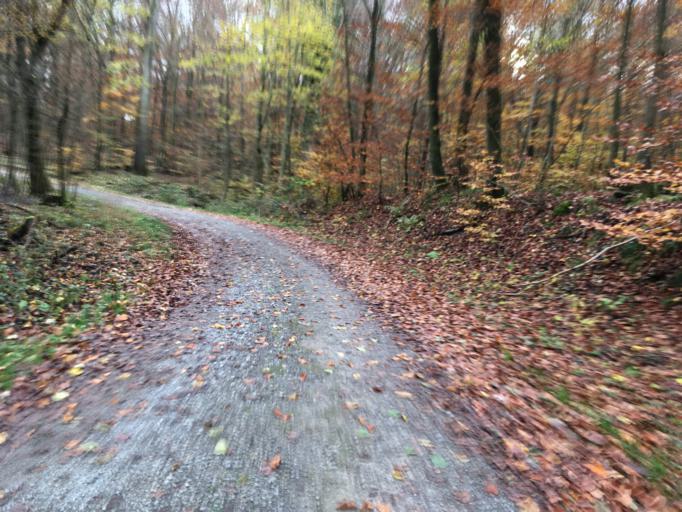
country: DE
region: Baden-Wuerttemberg
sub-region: Regierungsbezirk Stuttgart
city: Untergruppenbach
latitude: 49.0958
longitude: 9.2916
